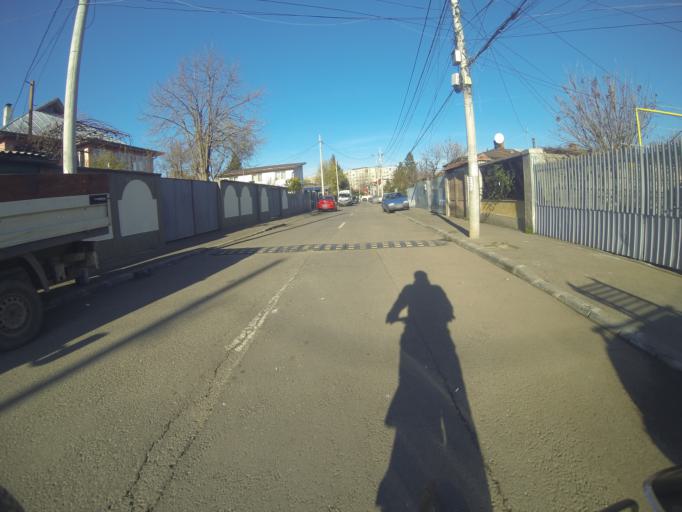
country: RO
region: Bucuresti
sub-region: Municipiul Bucuresti
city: Bucuresti
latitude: 44.4013
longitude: 26.0678
